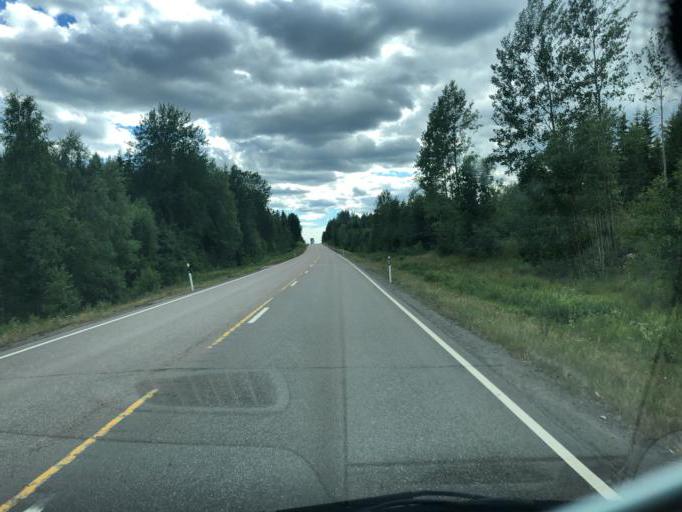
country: FI
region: Southern Savonia
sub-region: Mikkeli
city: Maentyharju
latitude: 61.0585
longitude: 27.0442
